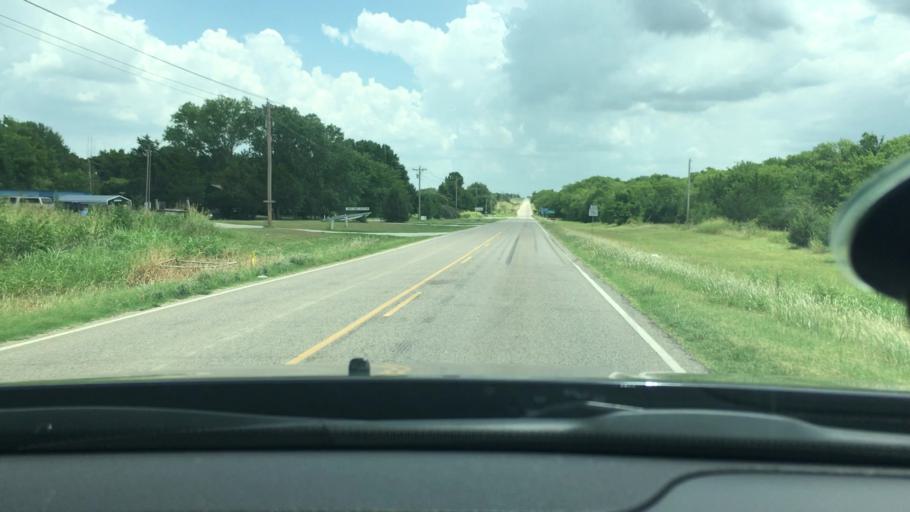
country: US
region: Oklahoma
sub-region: Love County
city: Marietta
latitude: 33.9404
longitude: -97.0957
